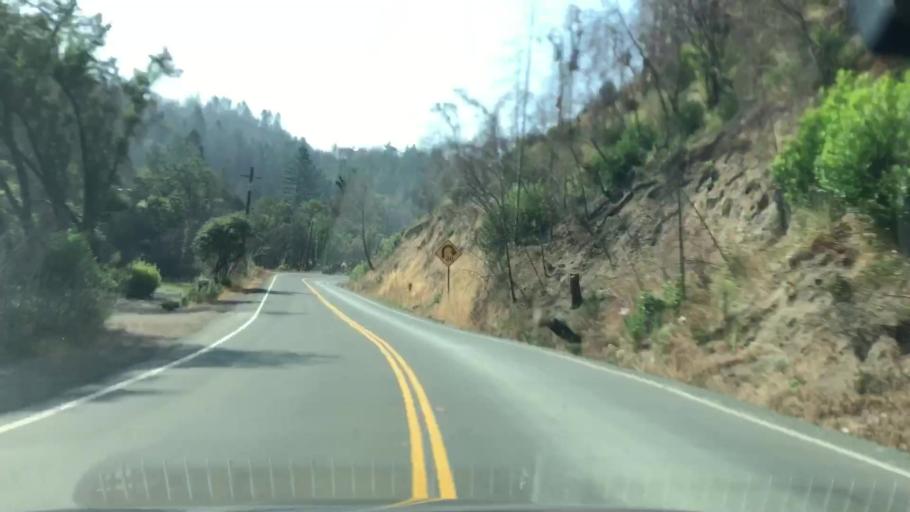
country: US
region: California
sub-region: Sonoma County
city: Larkfield-Wikiup
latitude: 38.5516
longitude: -122.6679
